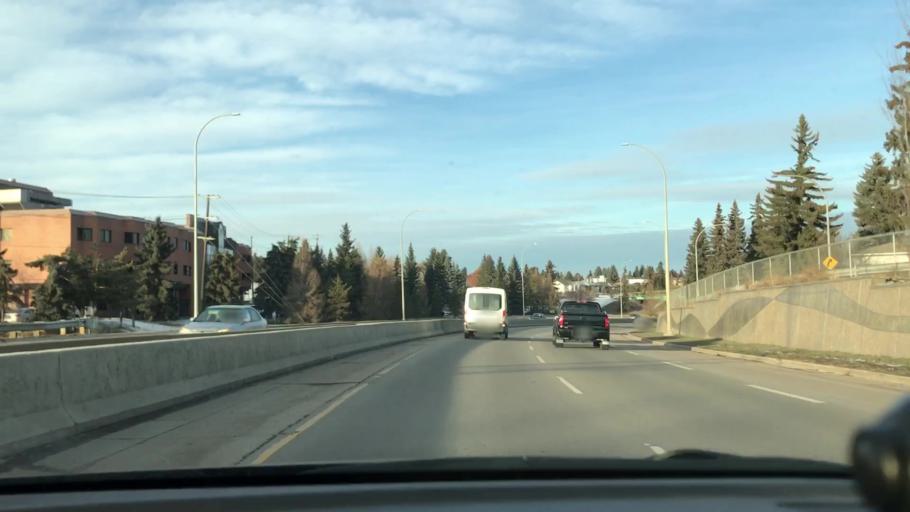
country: CA
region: Alberta
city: Edmonton
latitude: 53.5446
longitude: -113.4434
